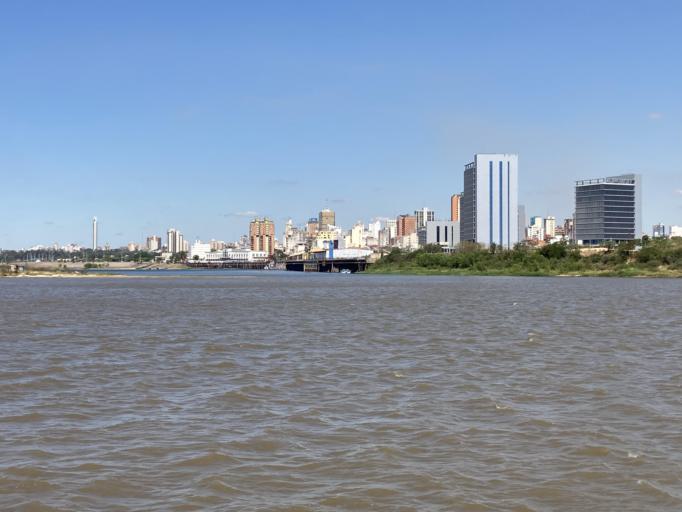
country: PY
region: Presidente Hayes
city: Nanawa
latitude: -25.2698
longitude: -57.6510
